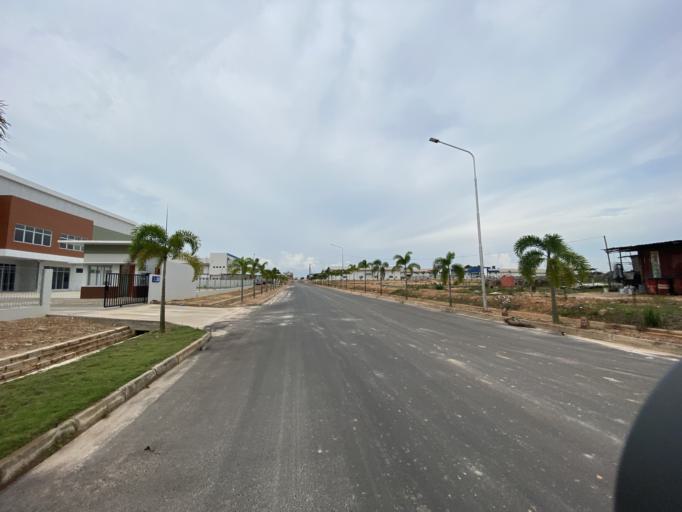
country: SG
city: Singapore
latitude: 1.0214
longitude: 103.9494
